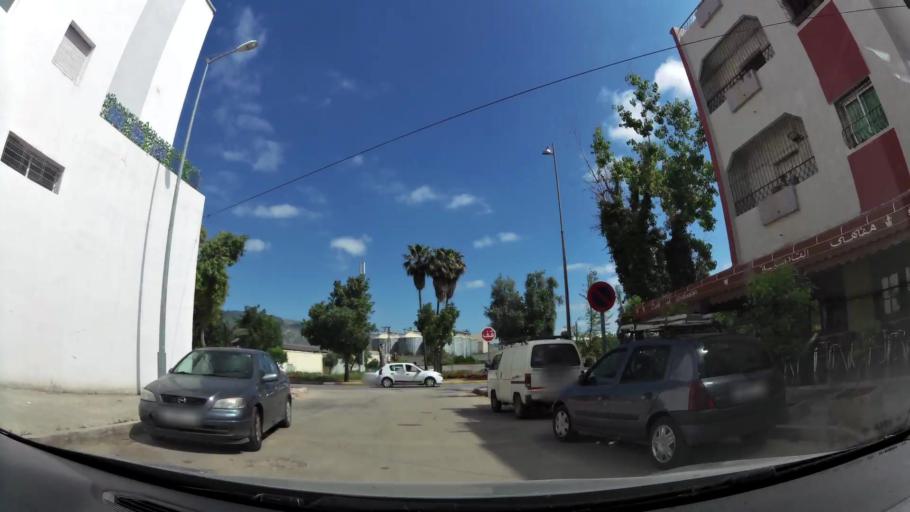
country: MA
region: Fes-Boulemane
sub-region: Fes
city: Fes
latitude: 34.0396
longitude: -5.0323
